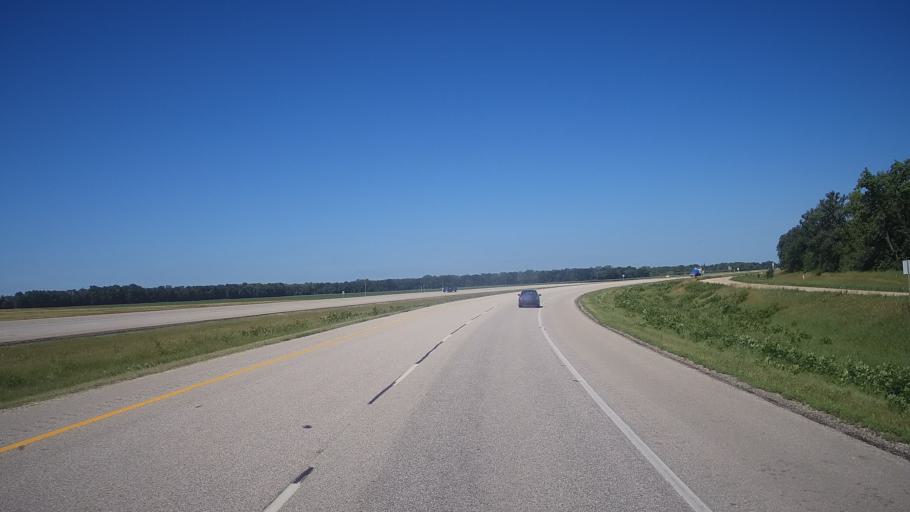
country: CA
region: Manitoba
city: Portage la Prairie
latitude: 49.9463
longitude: -98.2979
